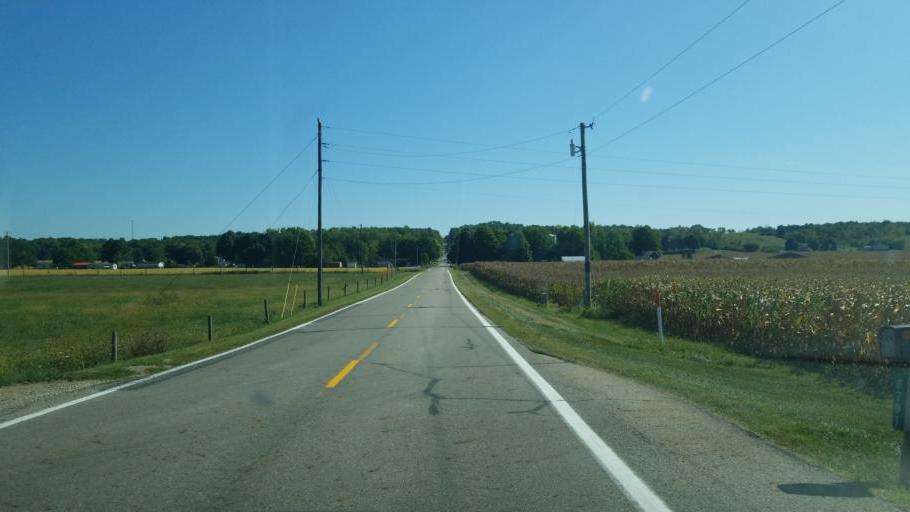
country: US
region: Ohio
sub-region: Champaign County
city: North Lewisburg
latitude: 40.2130
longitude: -83.6390
